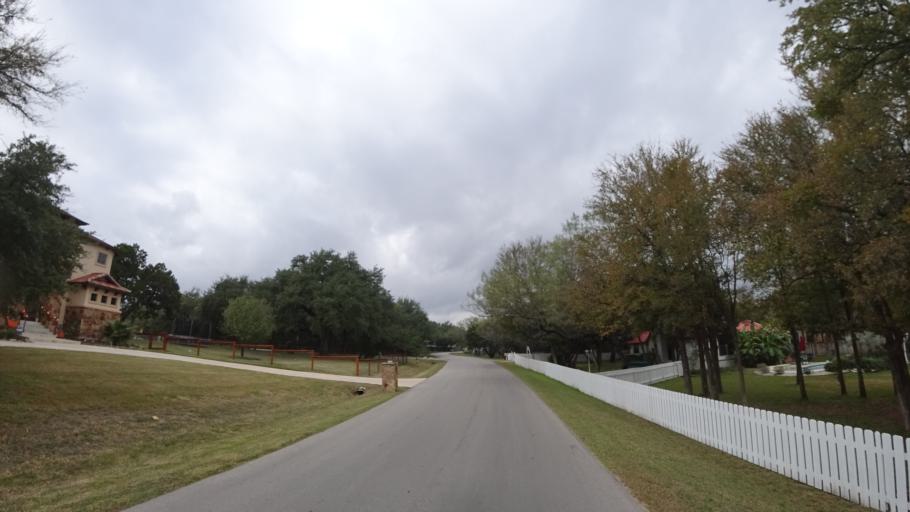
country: US
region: Texas
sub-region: Travis County
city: Bee Cave
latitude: 30.3321
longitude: -97.9219
